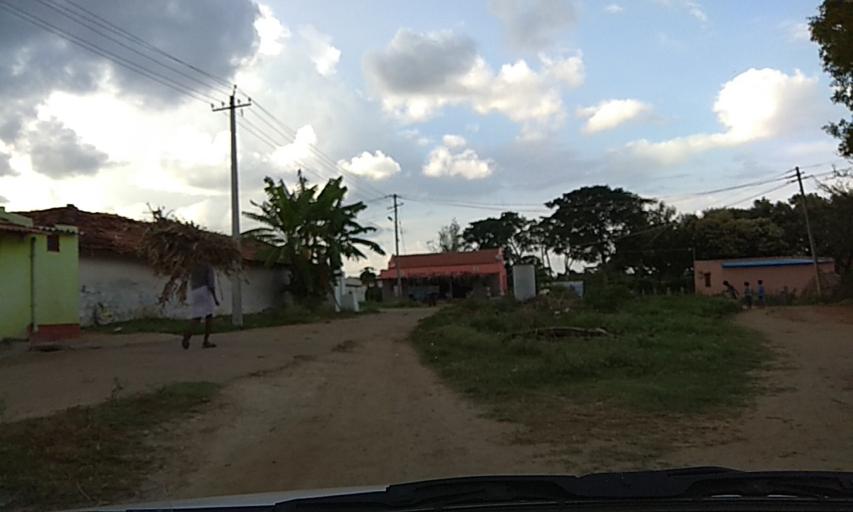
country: IN
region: Karnataka
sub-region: Chamrajnagar
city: Gundlupet
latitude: 11.8717
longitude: 76.7237
